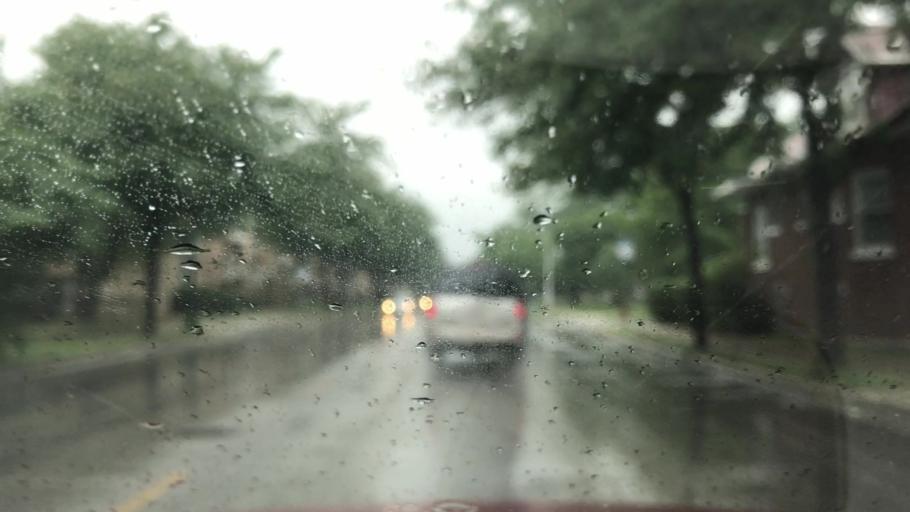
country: US
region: Illinois
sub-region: Cook County
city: Oak Park
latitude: 41.9037
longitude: -87.7558
